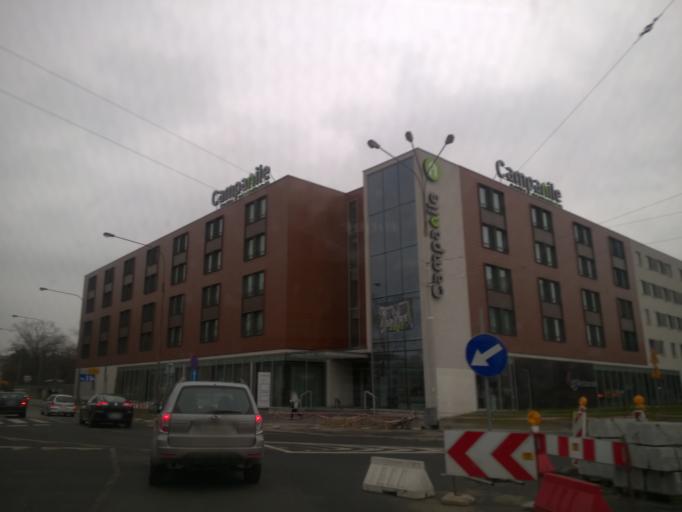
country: PL
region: Lower Silesian Voivodeship
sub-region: Powiat wroclawski
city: Wroclaw
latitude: 51.0947
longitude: 17.0311
